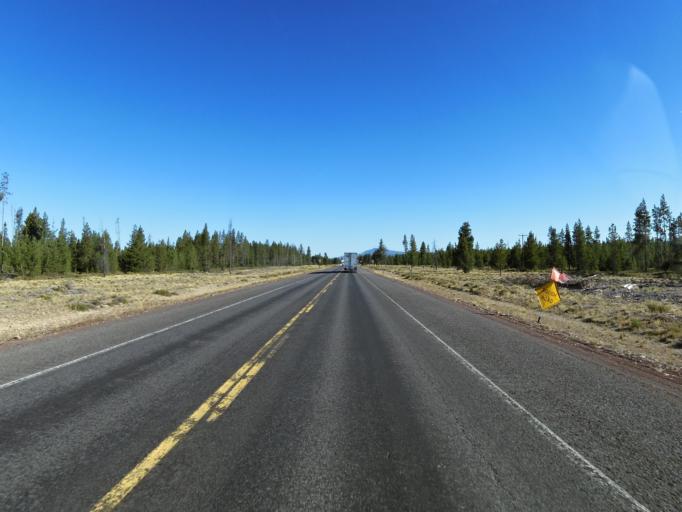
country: US
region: Oregon
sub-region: Deschutes County
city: La Pine
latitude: 43.1251
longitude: -121.8068
